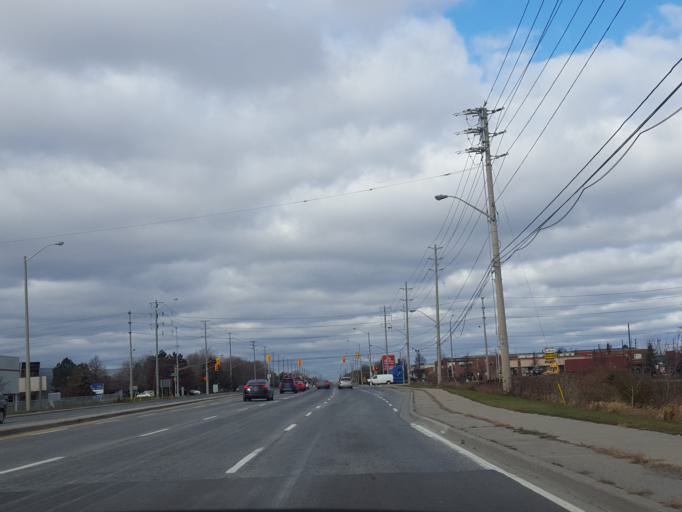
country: CA
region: Ontario
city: Brampton
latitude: 43.7295
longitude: -79.6770
